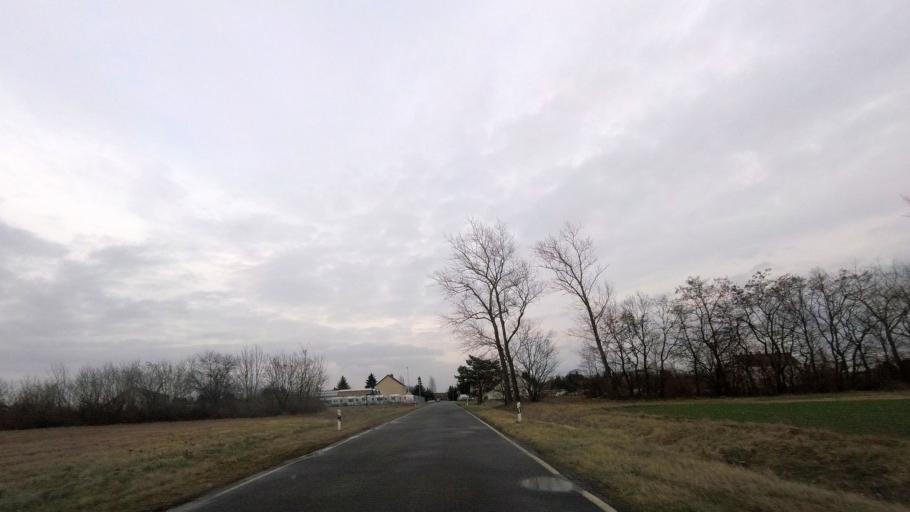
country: DE
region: Saxony-Anhalt
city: Seyda
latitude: 51.9163
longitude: 12.9585
